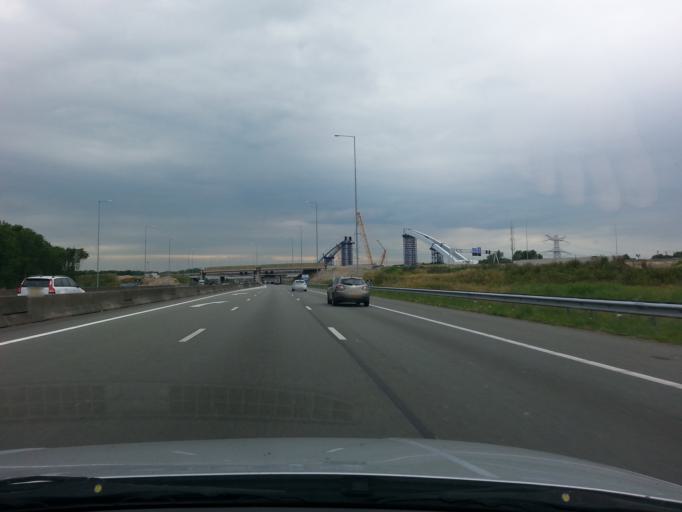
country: NL
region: North Holland
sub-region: Gemeente Naarden
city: Naarden
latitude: 52.3134
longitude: 5.1107
